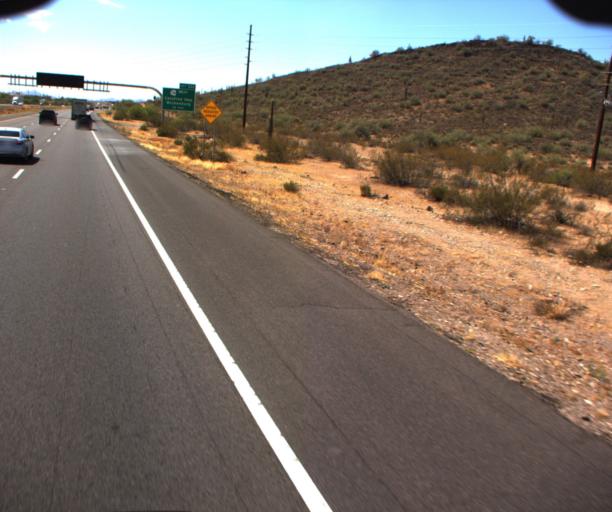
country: US
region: Arizona
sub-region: Maricopa County
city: Anthem
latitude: 33.8144
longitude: -112.1397
